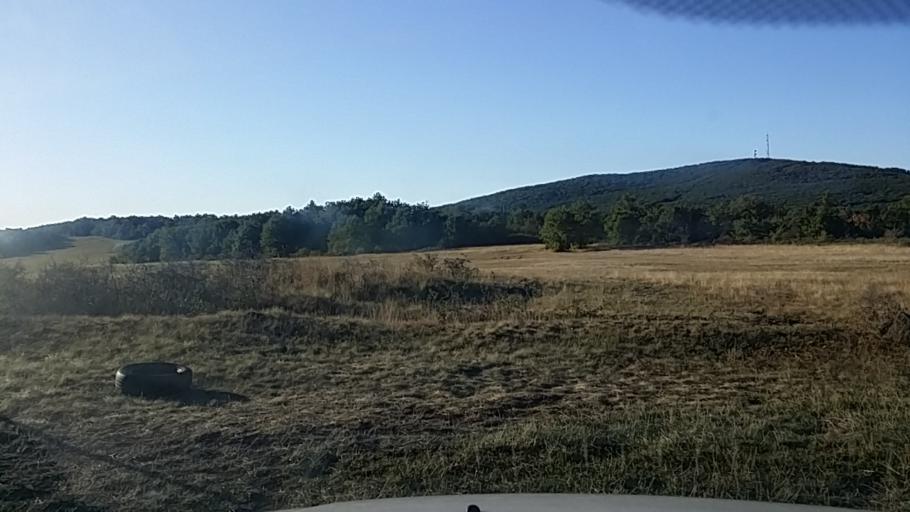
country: HU
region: Heves
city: Abasar
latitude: 47.8143
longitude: 19.9752
